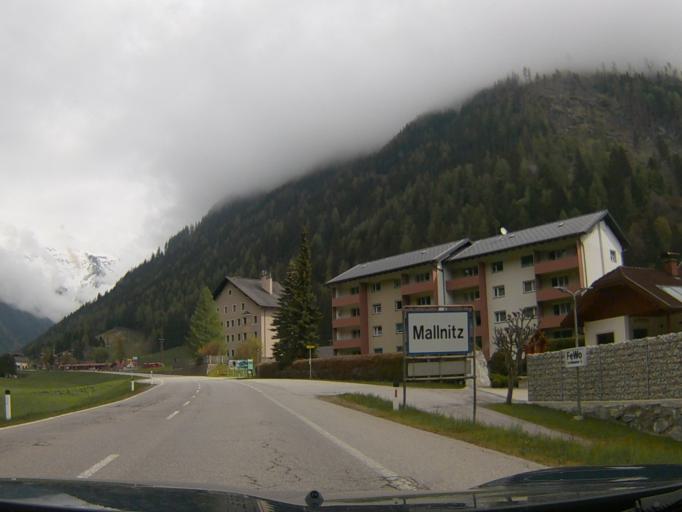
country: AT
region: Carinthia
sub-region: Politischer Bezirk Spittal an der Drau
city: Obervellach
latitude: 46.9772
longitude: 13.1769
